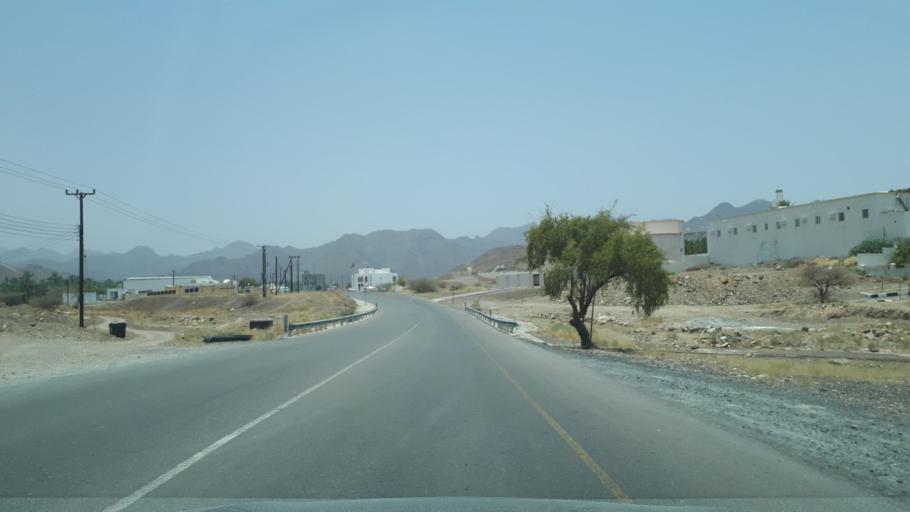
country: OM
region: Al Batinah
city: Rustaq
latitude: 23.4239
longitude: 57.2906
